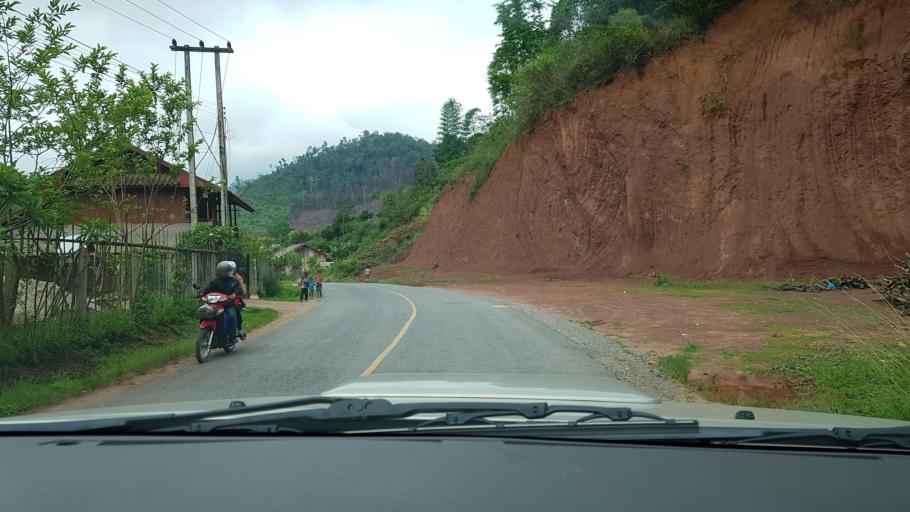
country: LA
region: Oudomxai
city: Muang Xay
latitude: 20.5837
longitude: 101.9221
